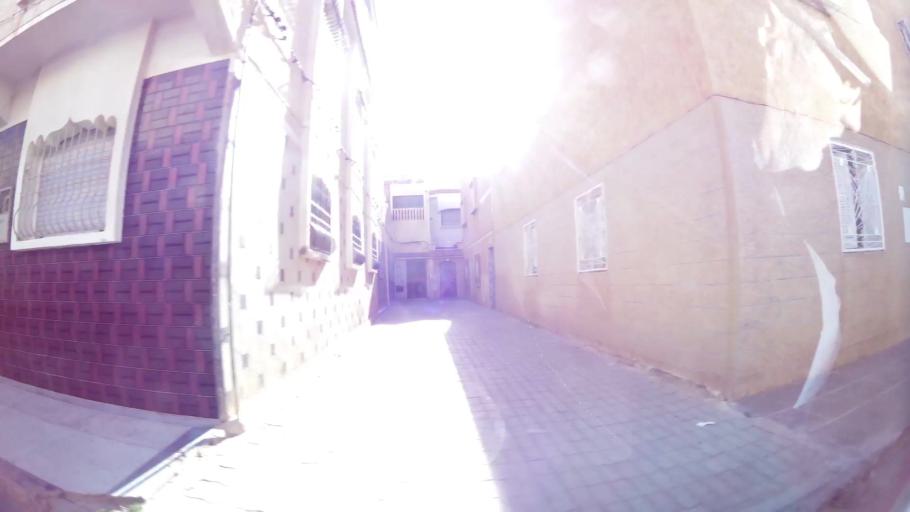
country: MA
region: Oriental
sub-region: Oujda-Angad
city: Oujda
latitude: 34.6733
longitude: -1.8960
